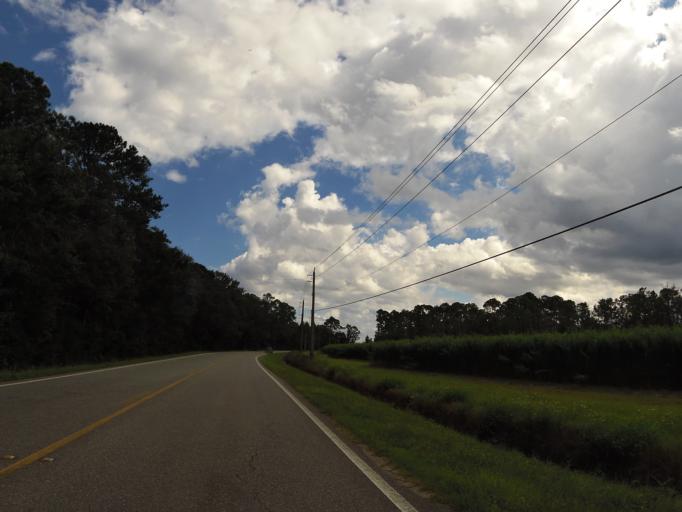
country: US
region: Florida
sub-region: Saint Johns County
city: Saint Augustine South
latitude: 29.8199
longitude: -81.4864
